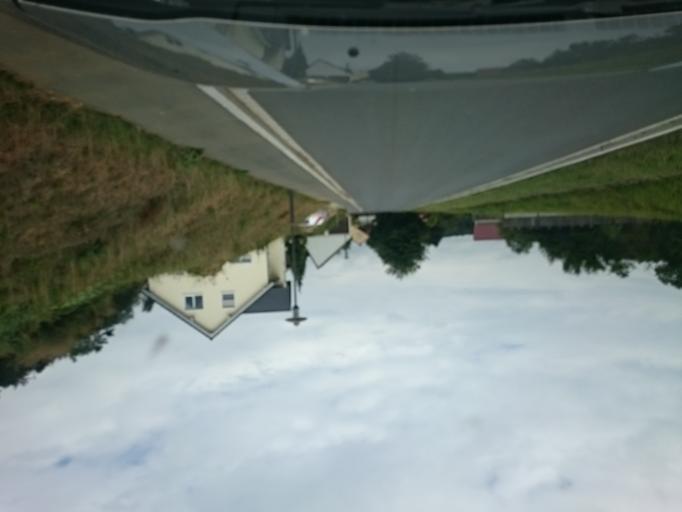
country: DE
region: Bavaria
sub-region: Regierungsbezirk Mittelfranken
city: Hartenstein
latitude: 49.5935
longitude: 11.5276
